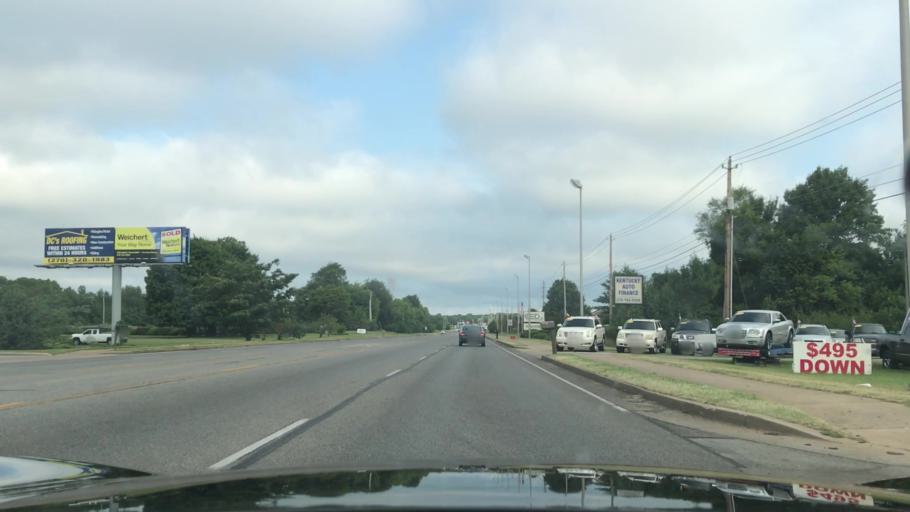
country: US
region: Kentucky
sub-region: Warren County
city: Bowling Green
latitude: 36.9531
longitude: -86.4430
